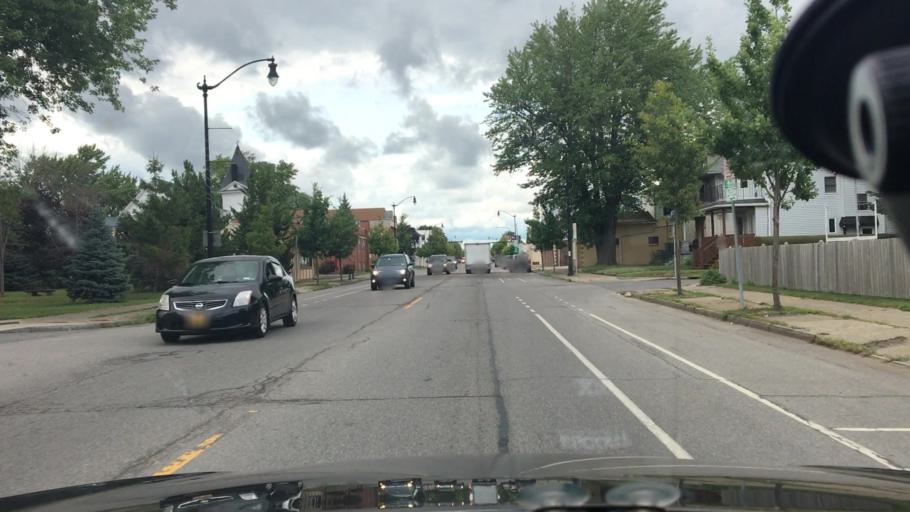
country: US
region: New York
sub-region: Erie County
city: Lackawanna
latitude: 42.8352
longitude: -78.8238
